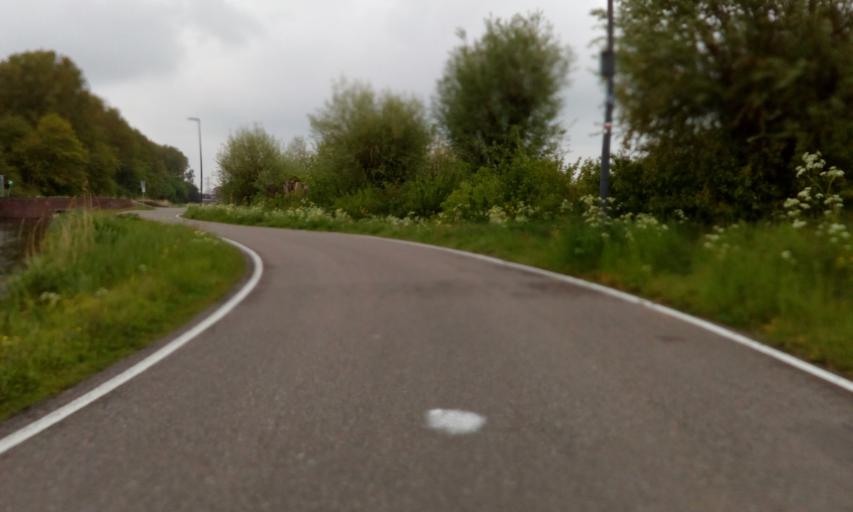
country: NL
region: South Holland
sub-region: Gemeente Schiedam
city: Schiedam
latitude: 51.9355
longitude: 4.4074
